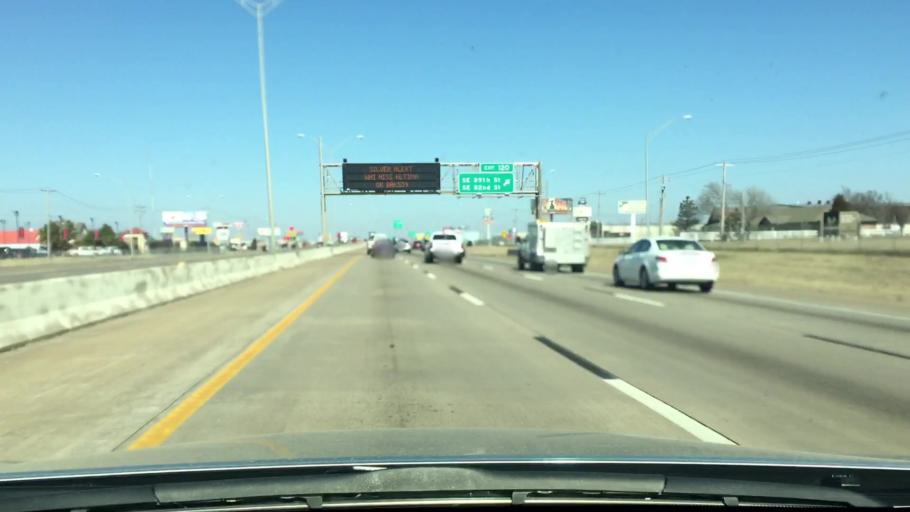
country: US
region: Oklahoma
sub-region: Cleveland County
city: Moore
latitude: 35.3725
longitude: -97.4949
